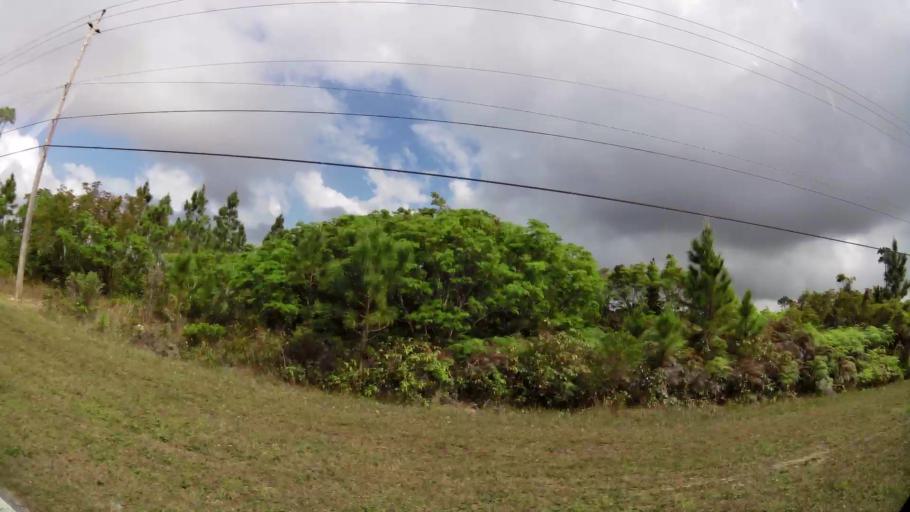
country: BS
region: Freeport
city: Lucaya
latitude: 26.5497
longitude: -78.5771
